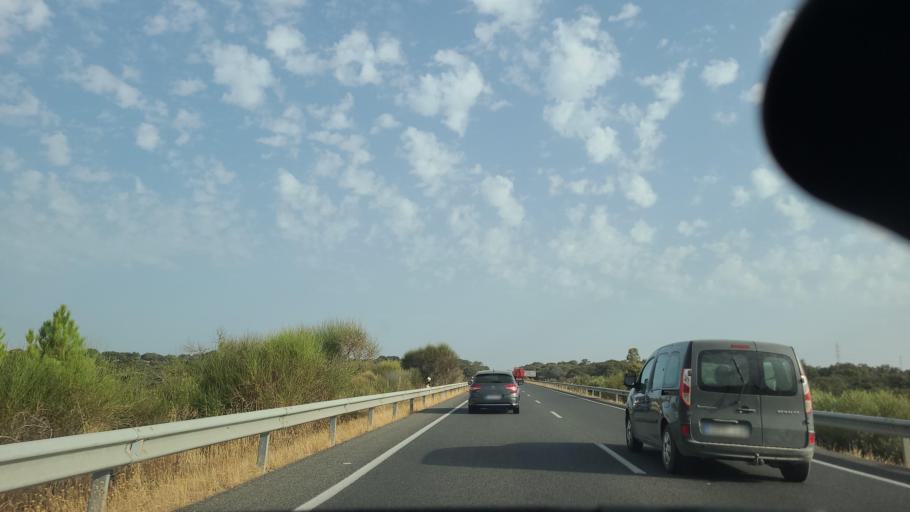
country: ES
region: Andalusia
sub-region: Province of Cordoba
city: Obejo
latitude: 38.0403
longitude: -4.8077
